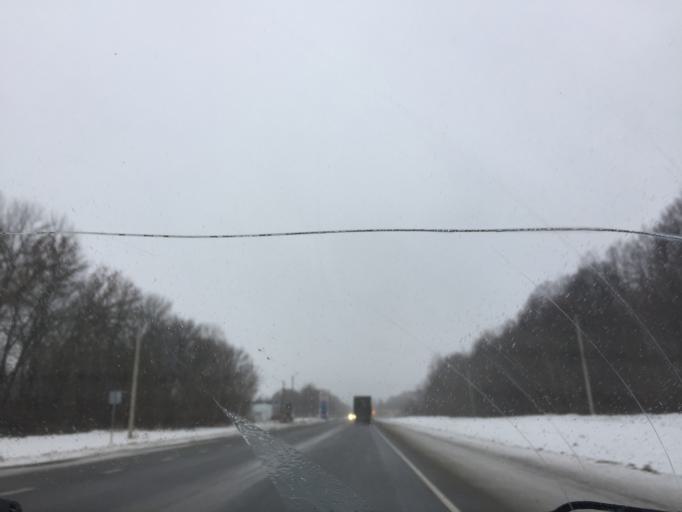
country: RU
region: Tula
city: Plavsk
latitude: 53.7483
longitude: 37.3252
